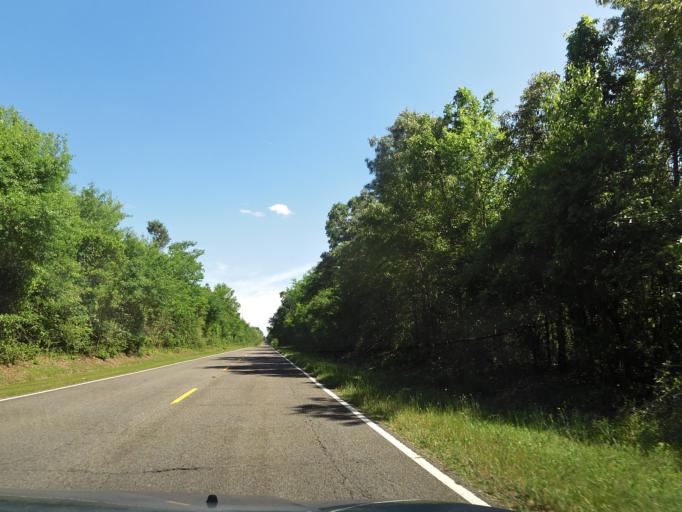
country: US
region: South Carolina
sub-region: Barnwell County
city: Williston
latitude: 33.4343
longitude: -81.4842
